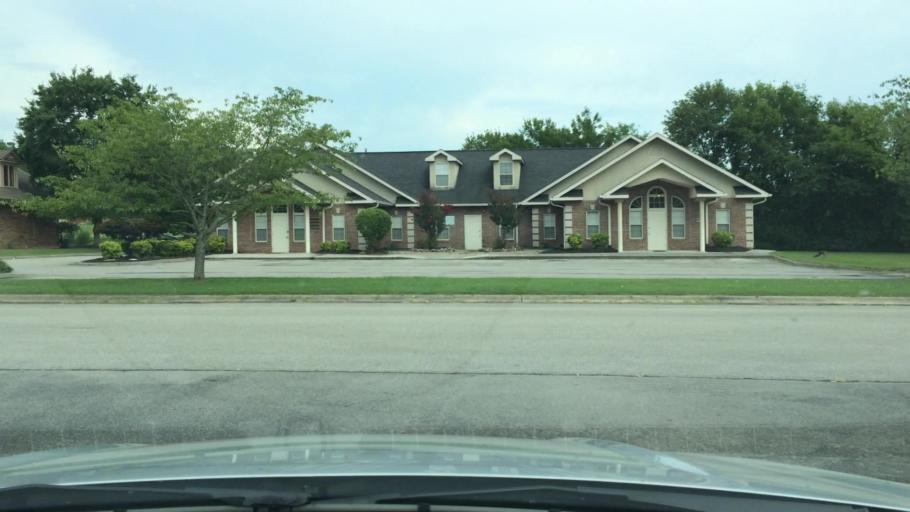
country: US
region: Tennessee
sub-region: Blount County
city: Maryville
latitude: 35.7534
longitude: -83.9525
